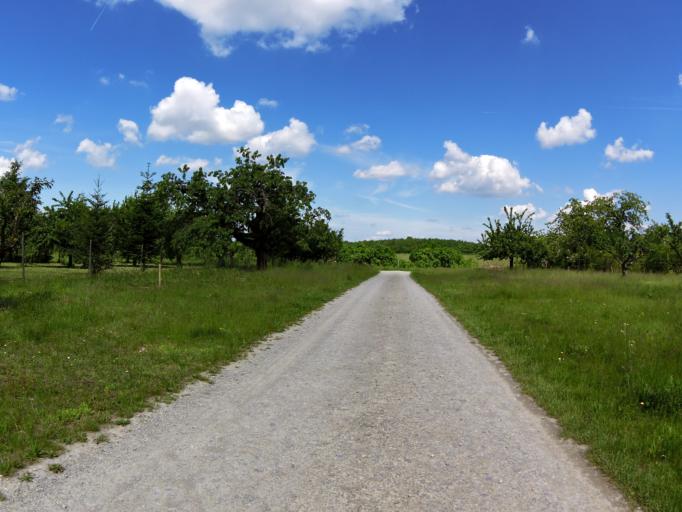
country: DE
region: Bavaria
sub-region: Regierungsbezirk Unterfranken
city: Winterhausen
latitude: 49.7276
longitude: 10.0223
